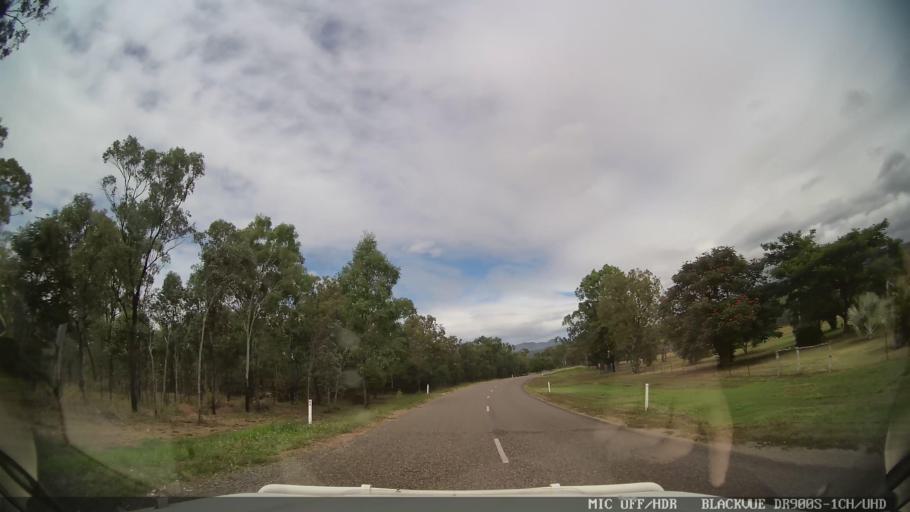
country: AU
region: Queensland
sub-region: Hinchinbrook
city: Ingham
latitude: -18.9537
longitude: 146.2909
